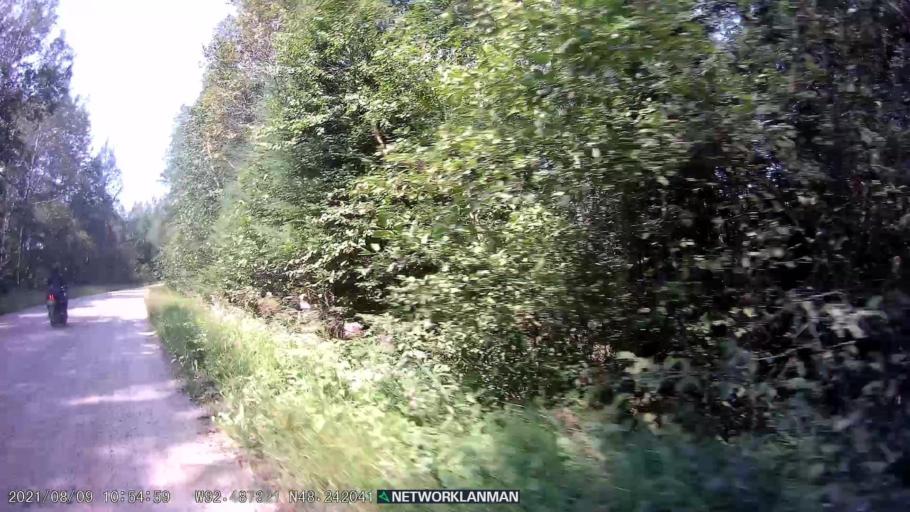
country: US
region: Minnesota
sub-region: Saint Louis County
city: Ely
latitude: 48.2420
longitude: -92.4874
